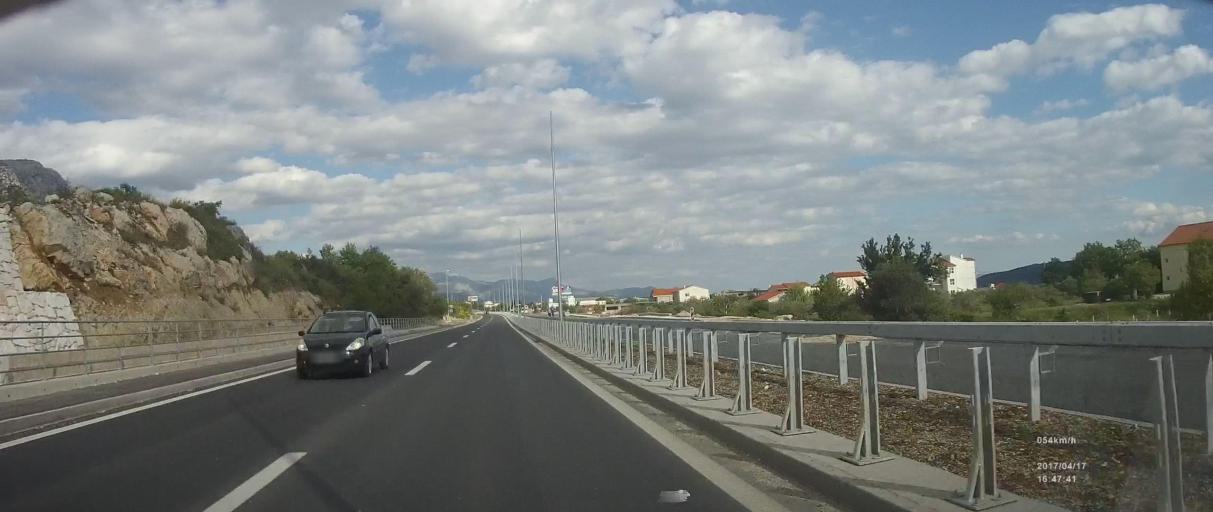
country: HR
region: Splitsko-Dalmatinska
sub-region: Grad Split
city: Split
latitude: 43.5582
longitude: 16.3691
